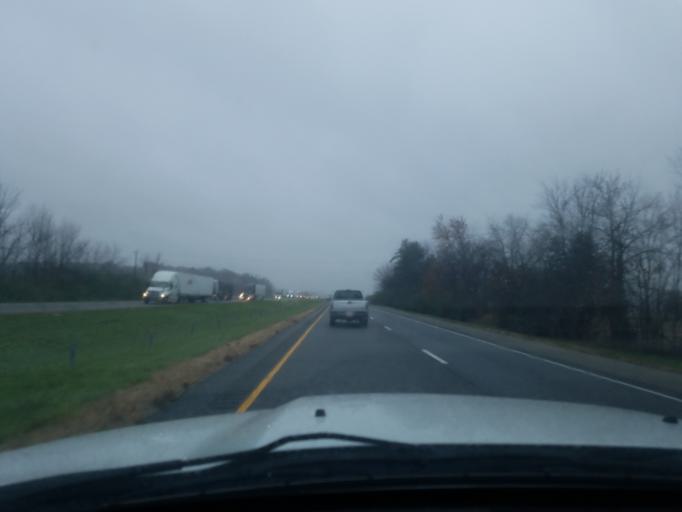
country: US
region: Indiana
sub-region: Grant County
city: Upland
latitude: 40.3908
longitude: -85.5487
